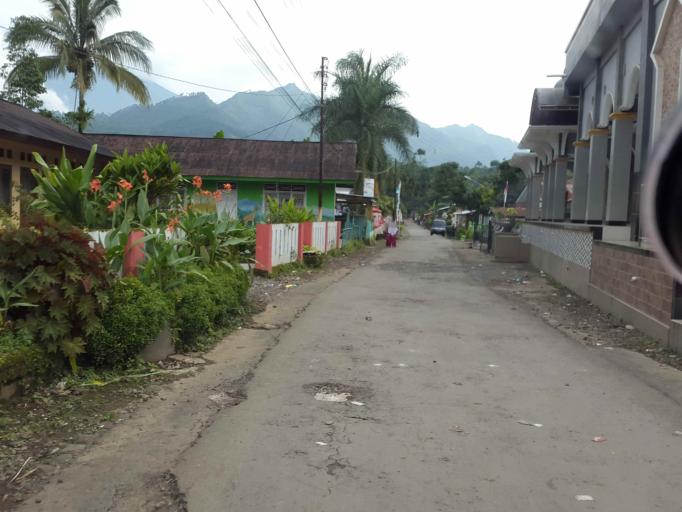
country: ID
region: Central Java
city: Randudongkal
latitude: -7.1858
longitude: 109.3298
